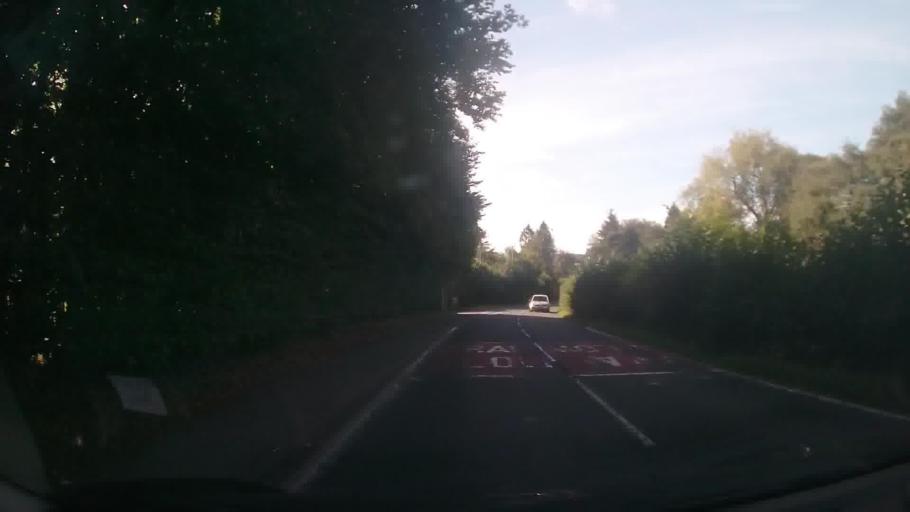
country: GB
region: Wales
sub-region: Blaenau Gwent
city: Brynmawr
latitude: 51.9040
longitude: -3.1938
